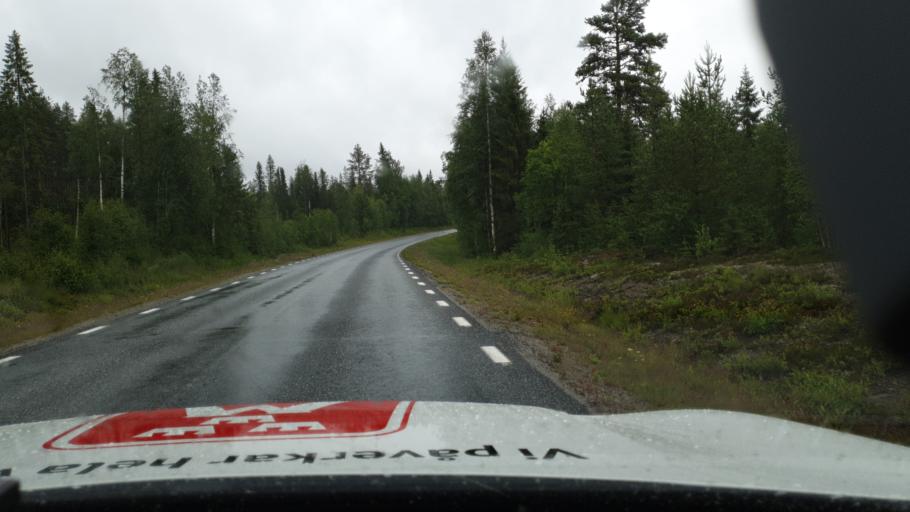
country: SE
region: Vaesterbotten
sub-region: Asele Kommun
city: Insjon
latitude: 64.3268
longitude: 17.7252
